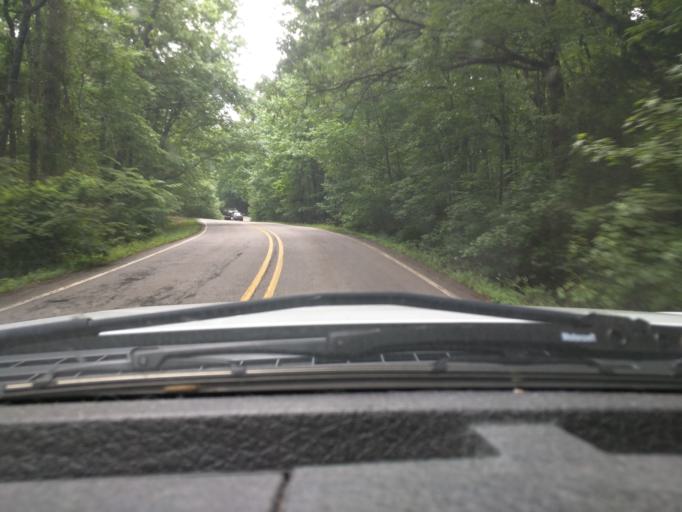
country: US
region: Arkansas
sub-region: Franklin County
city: Ozark
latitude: 35.7057
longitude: -93.8047
